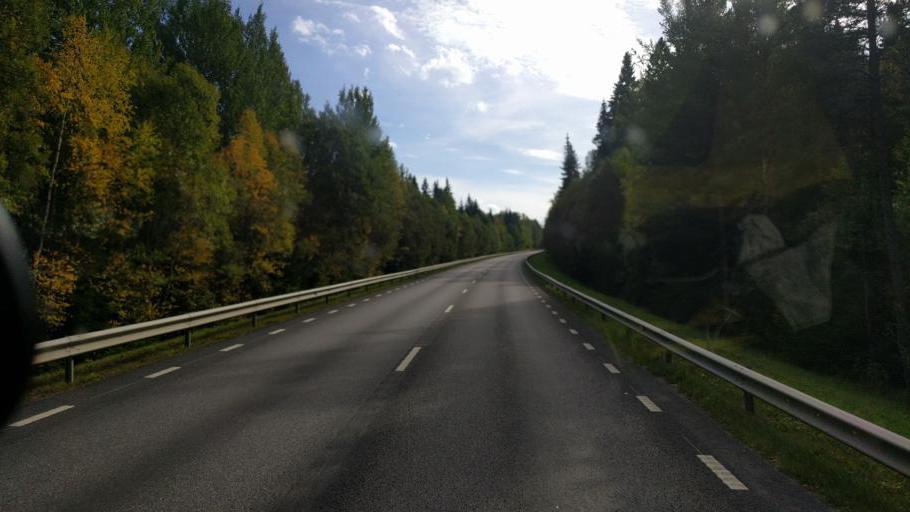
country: SE
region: OEstergoetland
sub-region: Kinda Kommun
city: Kisa
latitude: 57.9470
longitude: 15.6663
